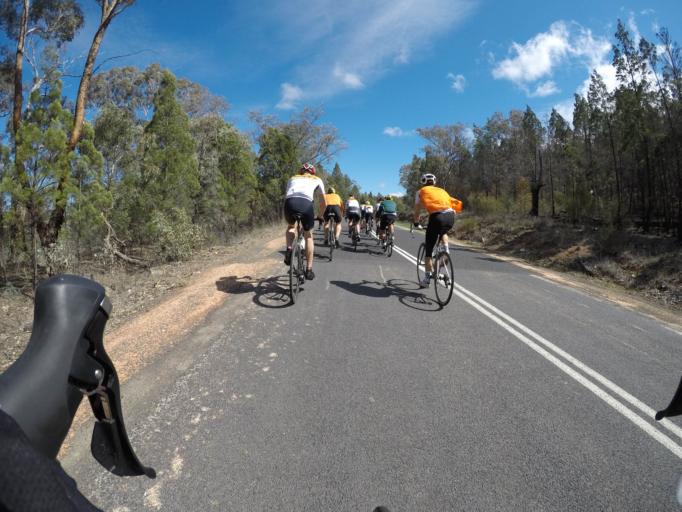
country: AU
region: New South Wales
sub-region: Parkes
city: Peak Hill
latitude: -32.6584
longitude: 148.5509
